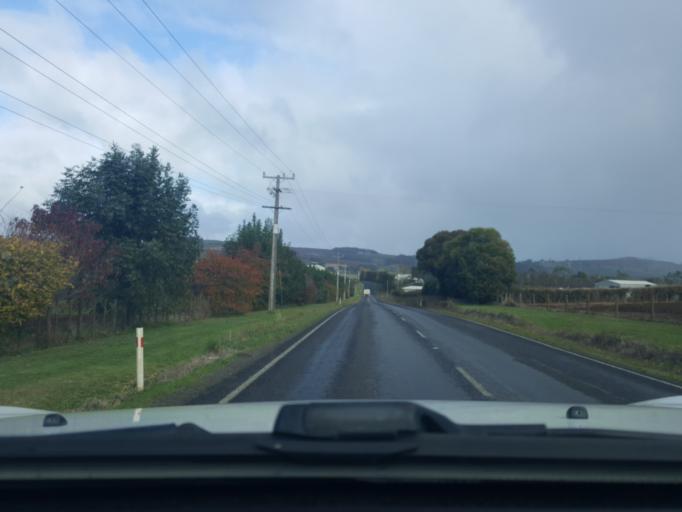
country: NZ
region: Auckland
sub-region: Auckland
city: Pukekohe East
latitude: -37.3020
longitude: 175.0199
